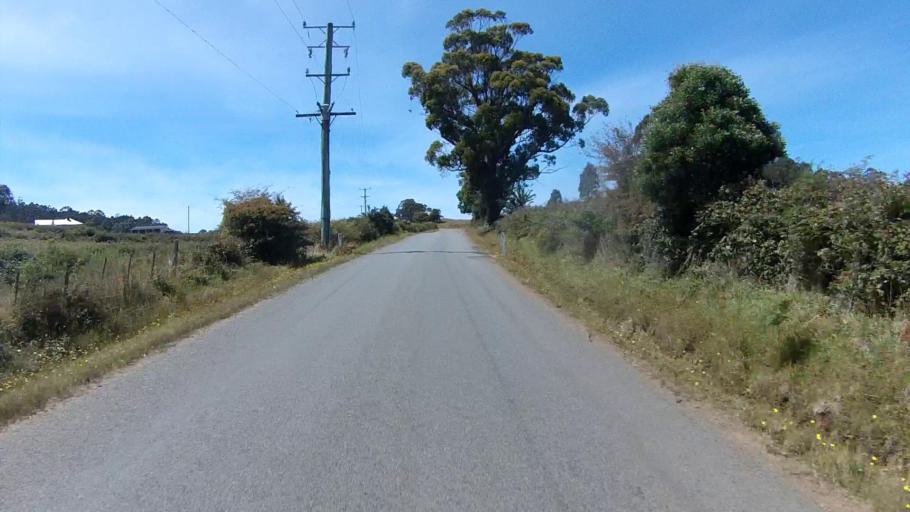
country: AU
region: Tasmania
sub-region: Sorell
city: Sorell
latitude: -42.7058
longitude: 147.7447
